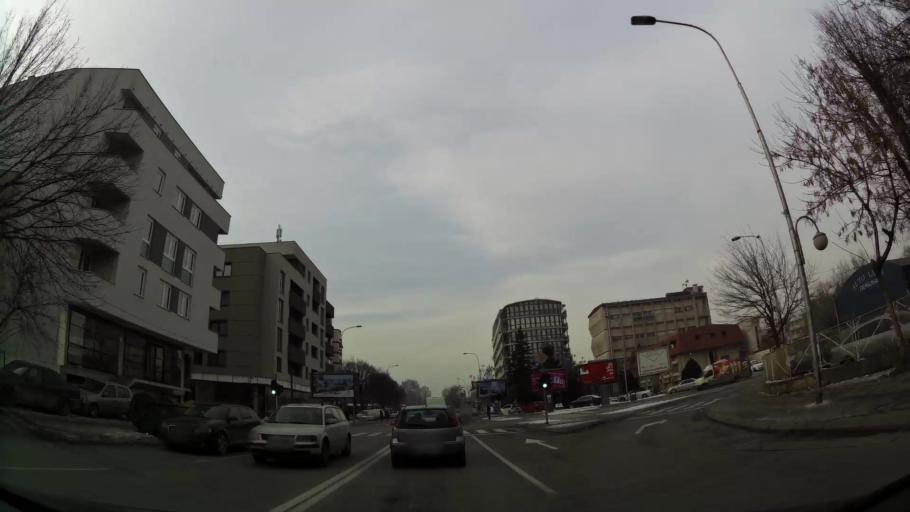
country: MK
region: Cair
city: Cair
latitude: 42.0139
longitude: 21.4441
